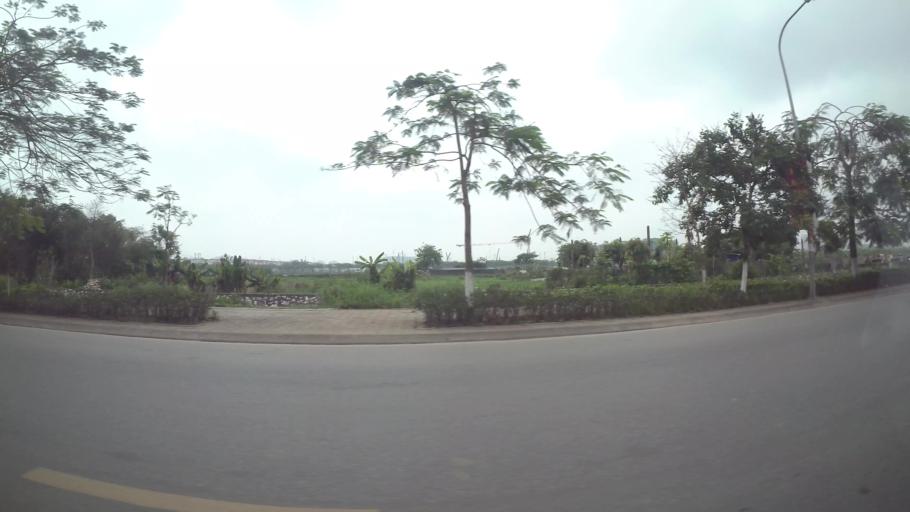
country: VN
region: Ha Noi
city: Trau Quy
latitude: 21.0507
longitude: 105.9215
